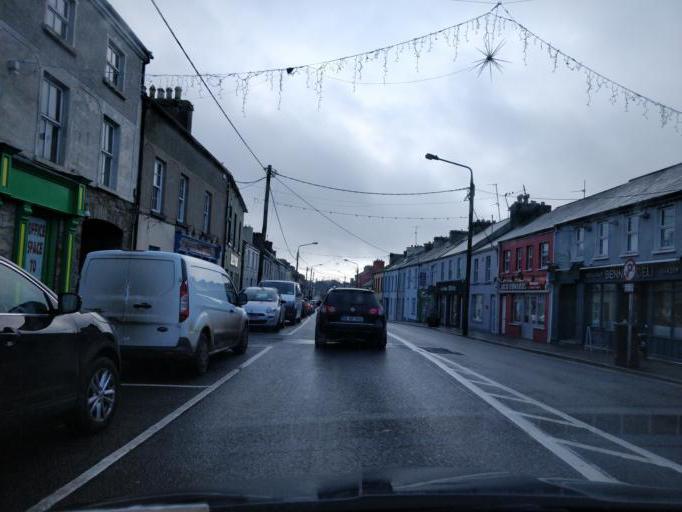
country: IE
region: Connaught
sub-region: Roscommon
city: Castlerea
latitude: 53.7695
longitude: -8.4949
